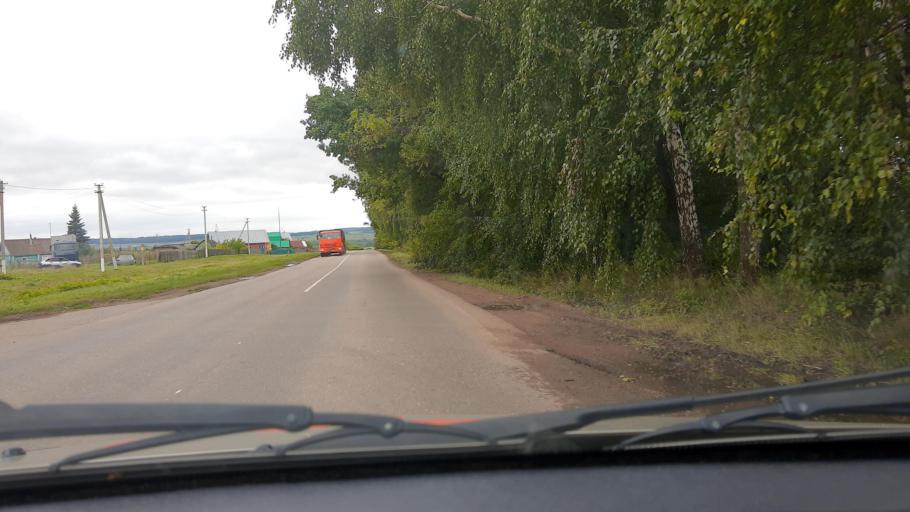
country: RU
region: Bashkortostan
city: Chishmy
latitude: 54.5994
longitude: 55.4432
